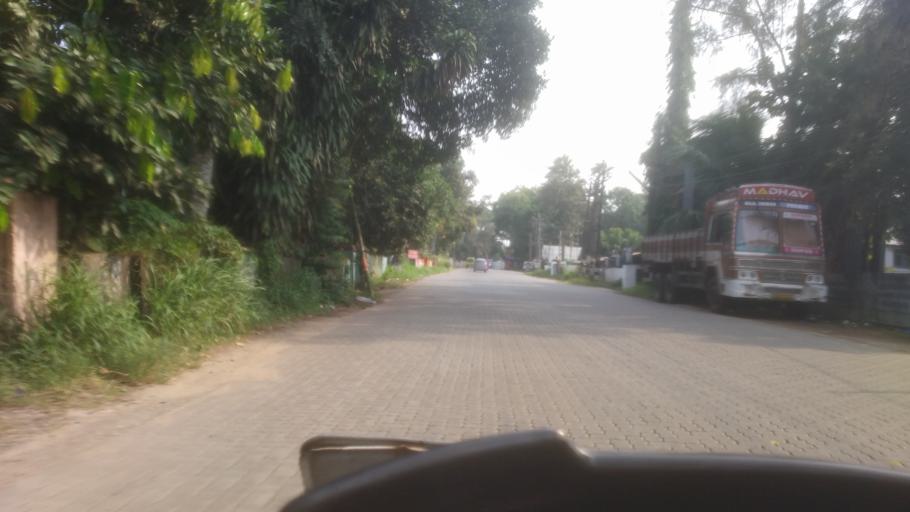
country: IN
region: Kerala
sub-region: Alappuzha
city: Arukutti
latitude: 9.9031
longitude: 76.3681
